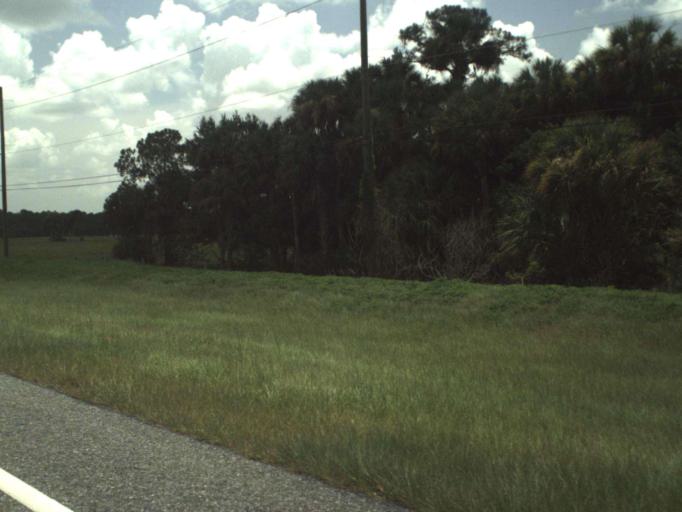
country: US
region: Florida
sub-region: Okeechobee County
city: Taylor Creek
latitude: 27.3663
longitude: -80.6064
